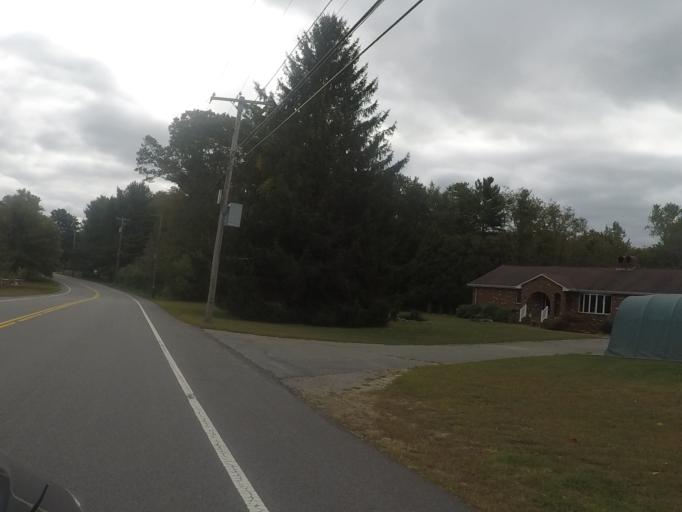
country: US
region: Massachusetts
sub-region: Bristol County
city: Smith Mills
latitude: 41.6827
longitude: -71.0222
